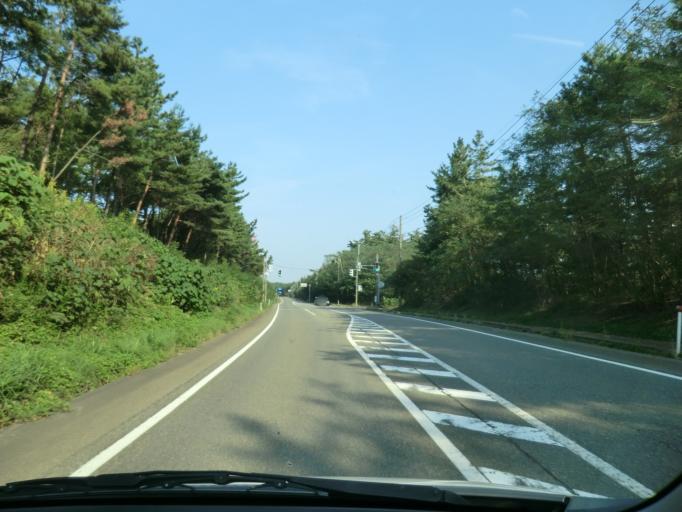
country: JP
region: Niigata
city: Kashiwazaki
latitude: 37.4172
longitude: 138.5949
